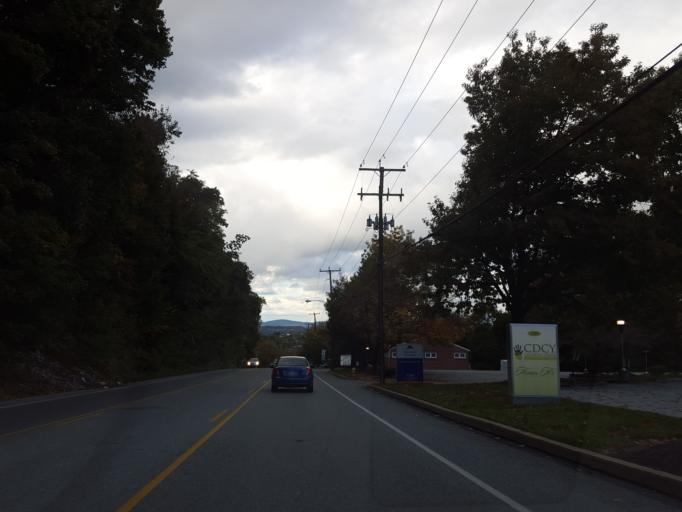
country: US
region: Pennsylvania
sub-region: York County
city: Valley View
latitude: 39.9464
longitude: -76.7095
